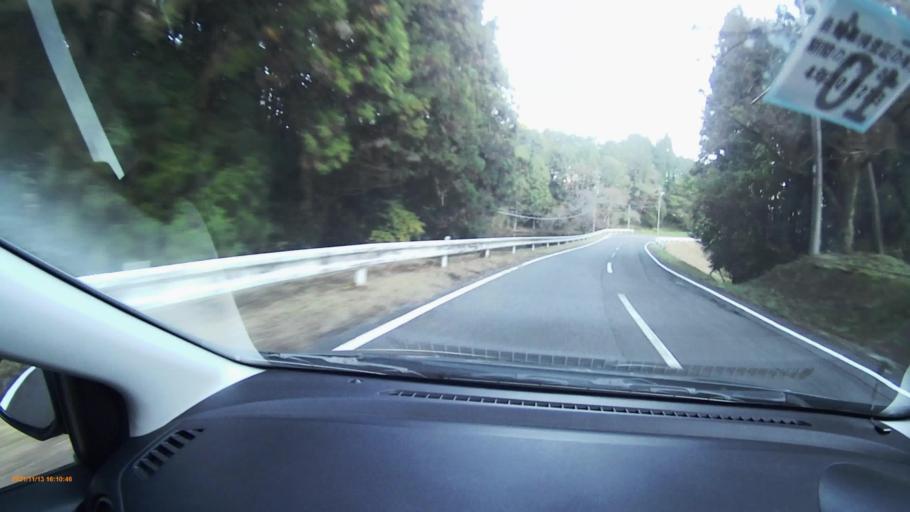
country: JP
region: Gifu
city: Nakatsugawa
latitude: 35.5881
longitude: 137.5021
